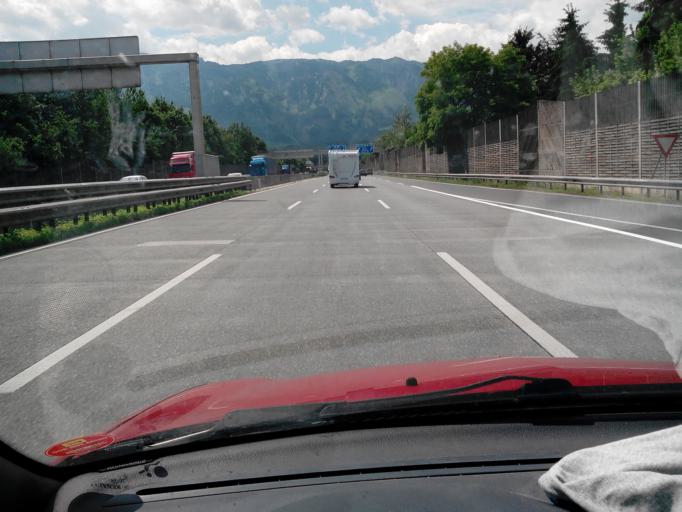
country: DE
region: Bavaria
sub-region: Upper Bavaria
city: Ainring
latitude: 47.7846
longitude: 12.9814
